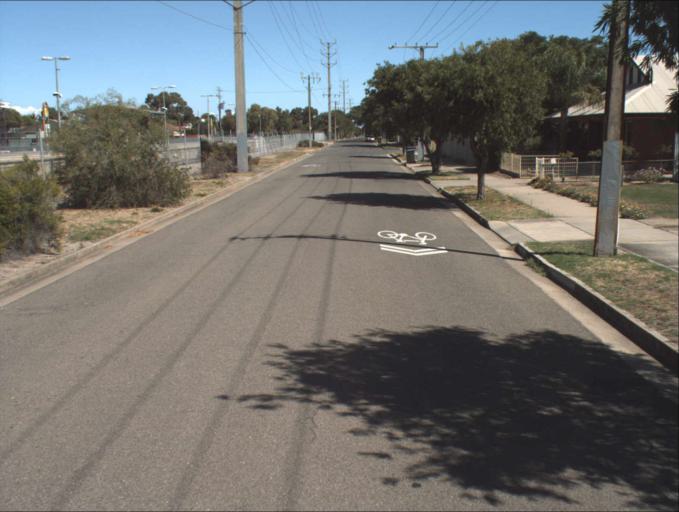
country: AU
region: South Australia
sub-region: Port Adelaide Enfield
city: Birkenhead
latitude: -34.8050
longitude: 138.4989
